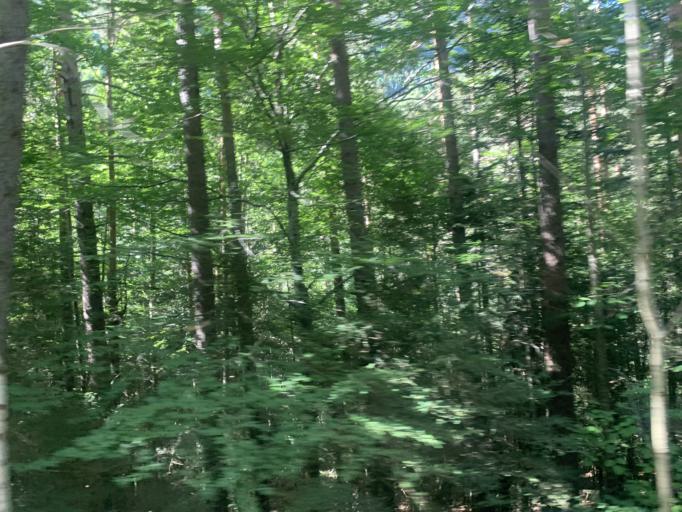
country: ES
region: Aragon
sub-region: Provincia de Huesca
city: Broto
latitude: 42.6531
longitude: -0.0767
